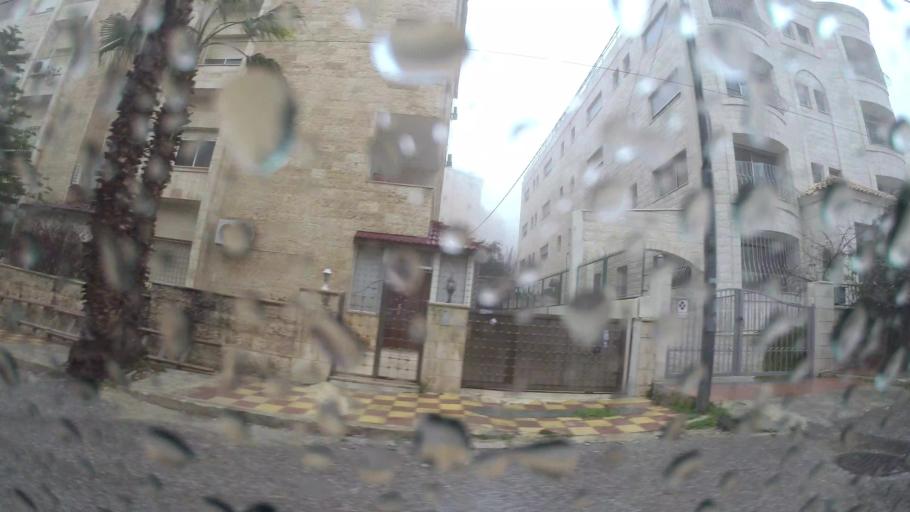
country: JO
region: Amman
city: Al Jubayhah
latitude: 32.0066
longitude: 35.8824
